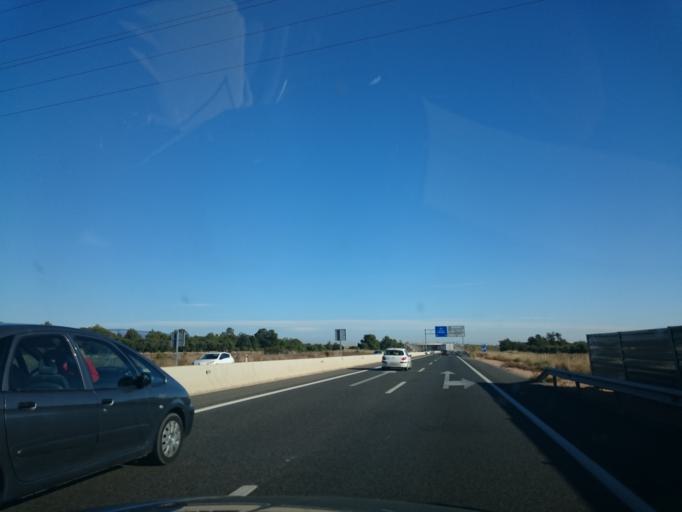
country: ES
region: Catalonia
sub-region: Provincia de Tarragona
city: Cambrils
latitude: 41.0535
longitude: 0.9839
